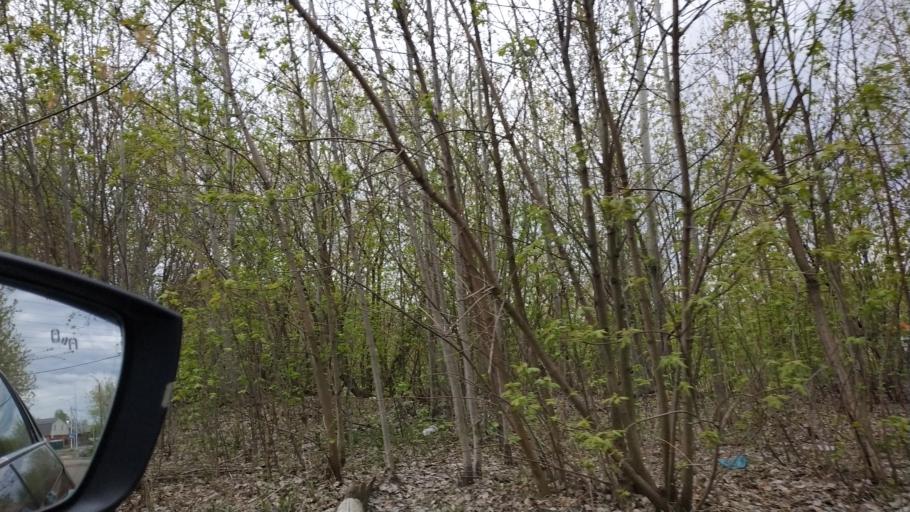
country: RU
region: Moskovskaya
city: Pavlovskiy Posad
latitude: 55.7853
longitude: 38.6868
